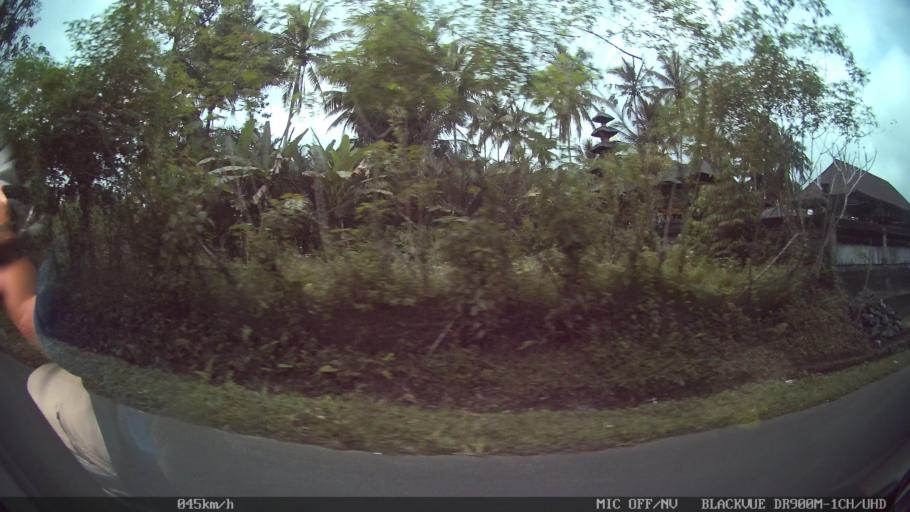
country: ID
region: Bali
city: Banjar Geriana Kangin
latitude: -8.4113
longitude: 115.4384
